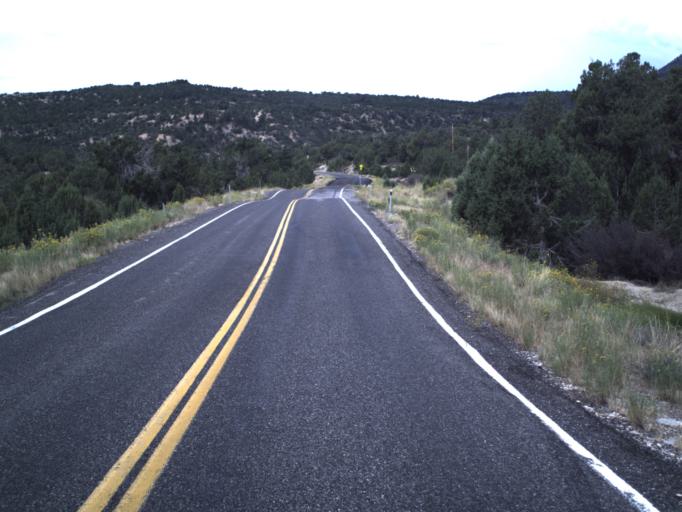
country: US
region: Utah
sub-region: Washington County
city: Hildale
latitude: 37.2620
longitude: -112.7841
